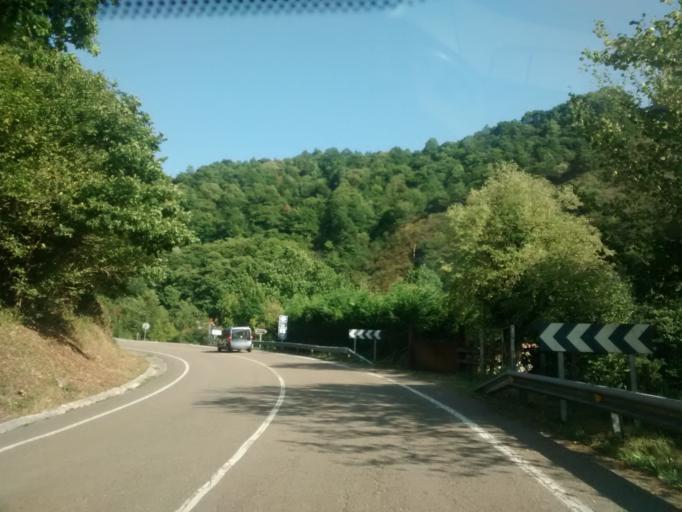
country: ES
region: Cantabria
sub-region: Provincia de Cantabria
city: Ruente
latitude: 43.1603
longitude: -4.2510
